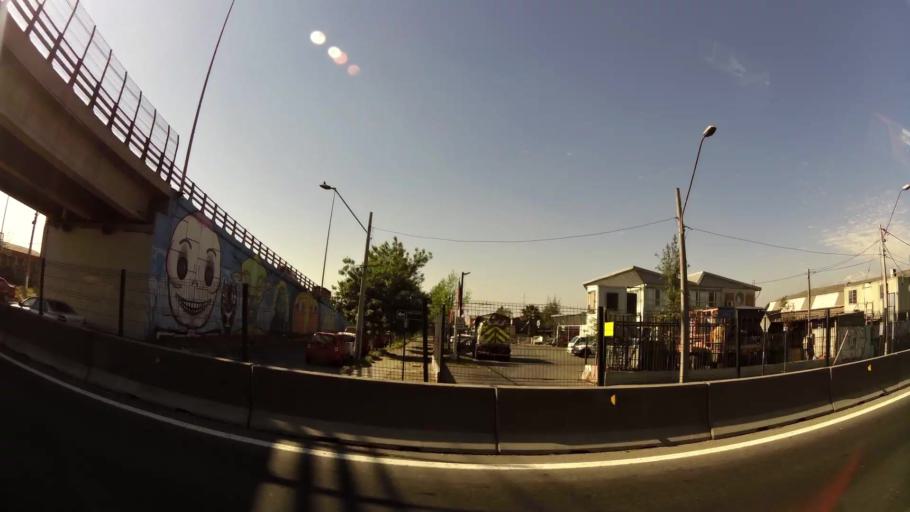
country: CL
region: Santiago Metropolitan
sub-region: Provincia de Maipo
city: San Bernardo
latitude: -33.5340
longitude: -70.6751
